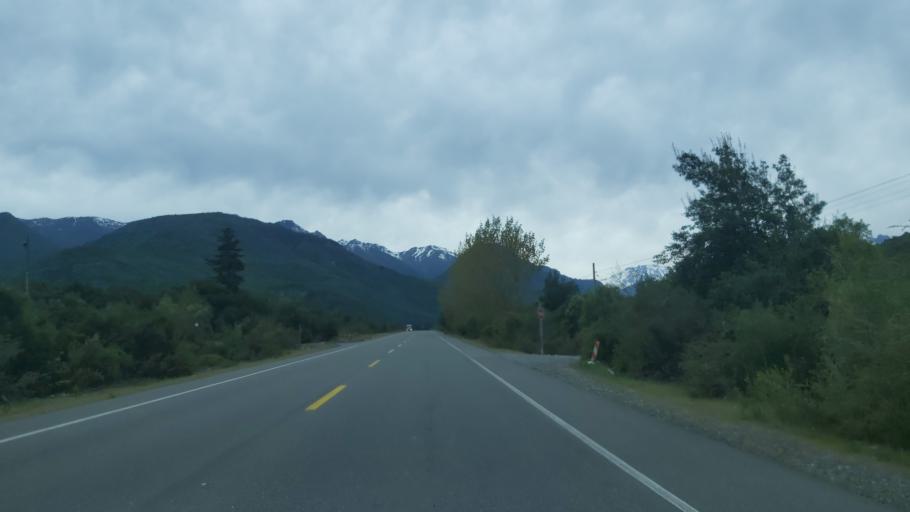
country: CL
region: Maule
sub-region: Provincia de Linares
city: Colbun
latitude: -35.7146
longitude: -71.1147
